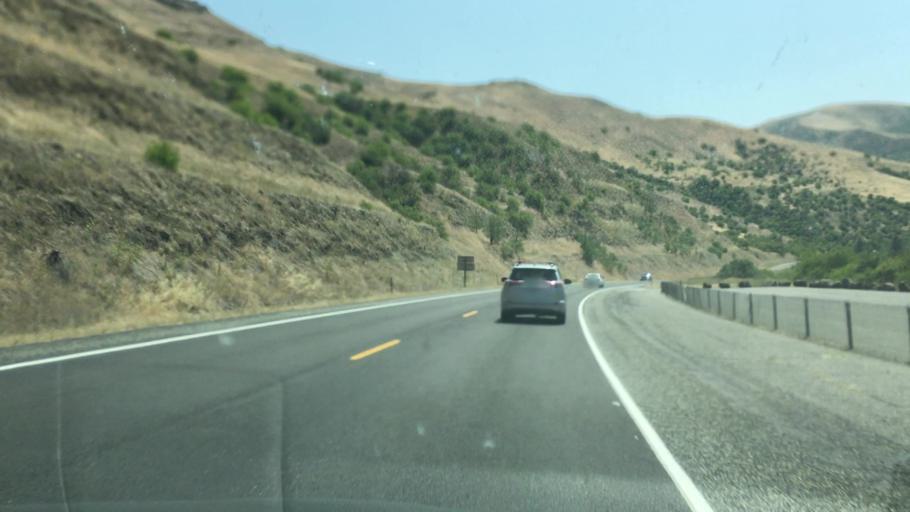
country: US
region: Idaho
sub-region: Idaho County
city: Grangeville
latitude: 45.7339
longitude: -116.3040
